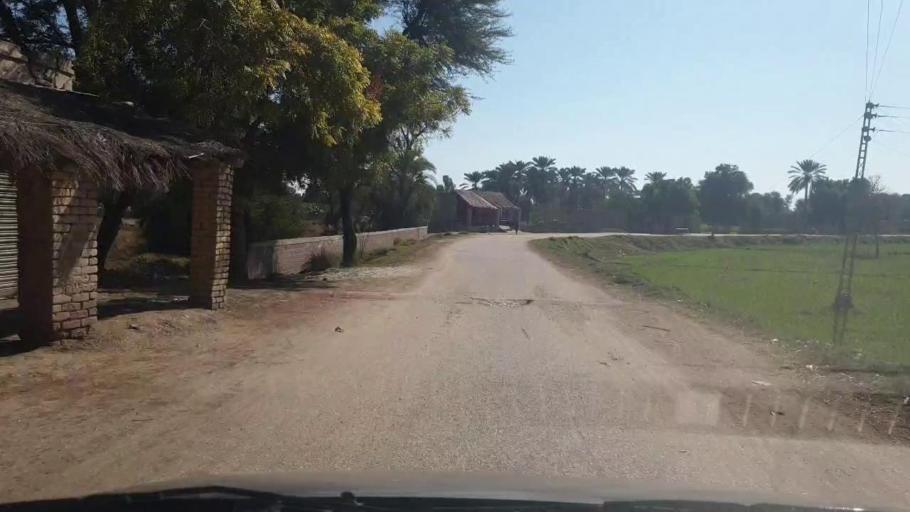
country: PK
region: Sindh
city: Bozdar
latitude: 27.1176
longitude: 68.6346
